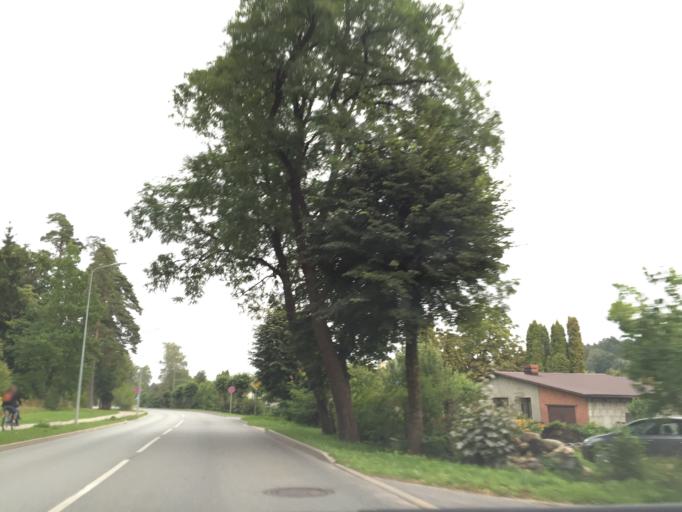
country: LV
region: Ogre
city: Ogre
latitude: 56.8161
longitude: 24.6212
